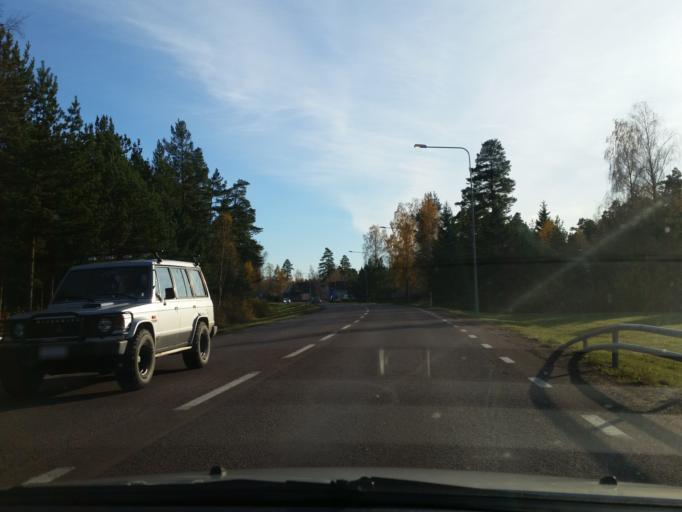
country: AX
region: Mariehamns stad
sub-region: Mariehamn
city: Mariehamn
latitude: 60.1220
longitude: 19.9341
